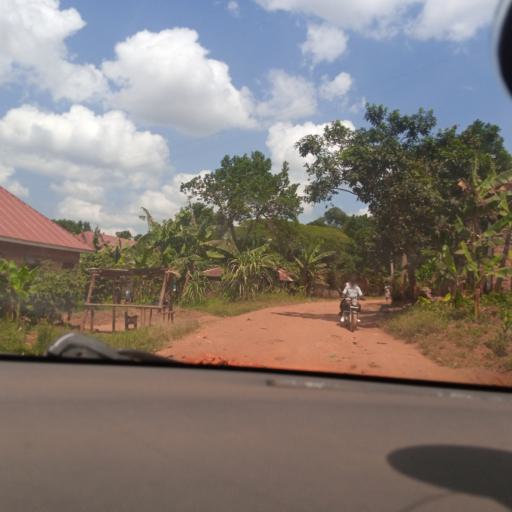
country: UG
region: Central Region
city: Masaka
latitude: -0.3290
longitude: 31.7409
